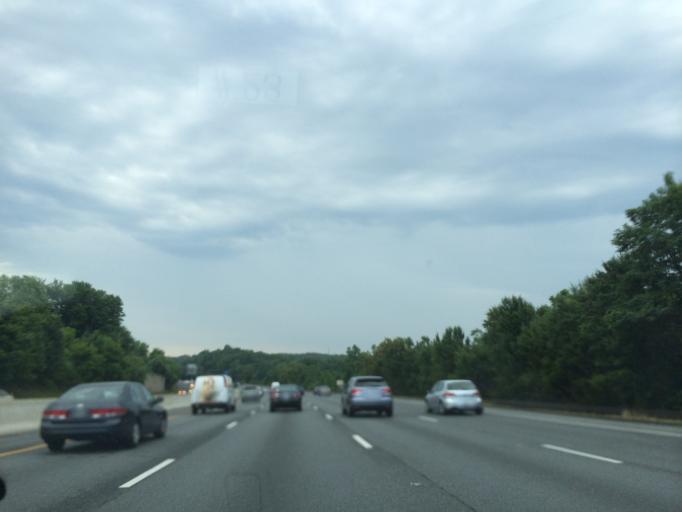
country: US
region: Maryland
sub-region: Montgomery County
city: Germantown
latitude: 39.1690
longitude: -77.2430
